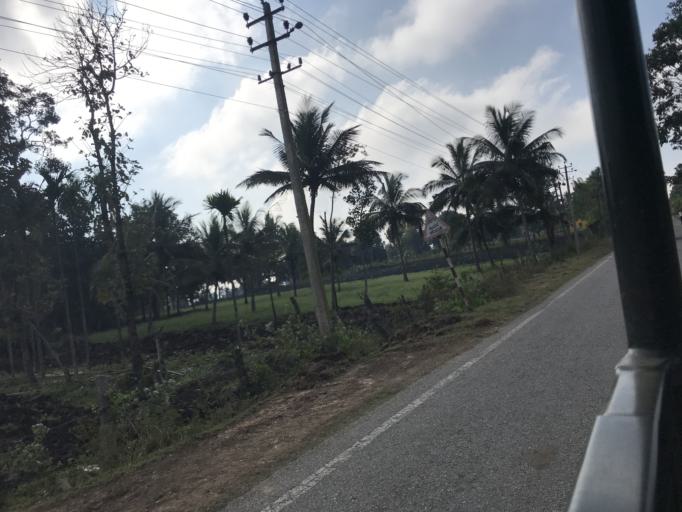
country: IN
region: Karnataka
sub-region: Mysore
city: Heggadadevankote
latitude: 11.9452
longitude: 76.2466
